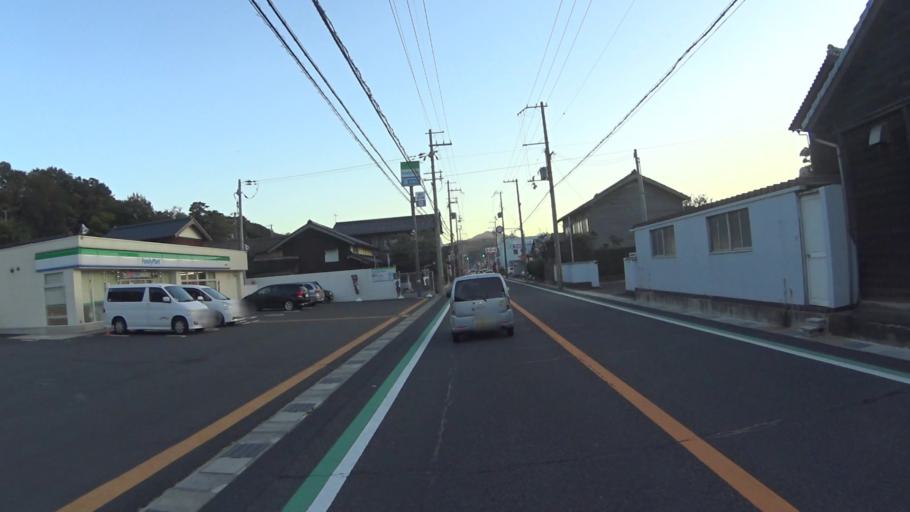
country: JP
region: Kyoto
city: Miyazu
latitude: 35.6765
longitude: 135.0283
